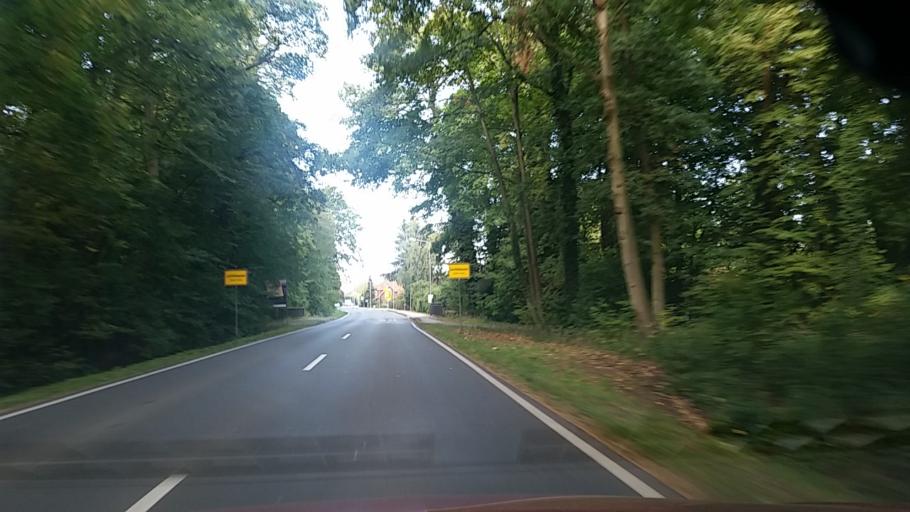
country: DE
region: Lower Saxony
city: Celle
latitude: 52.6231
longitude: 10.1354
